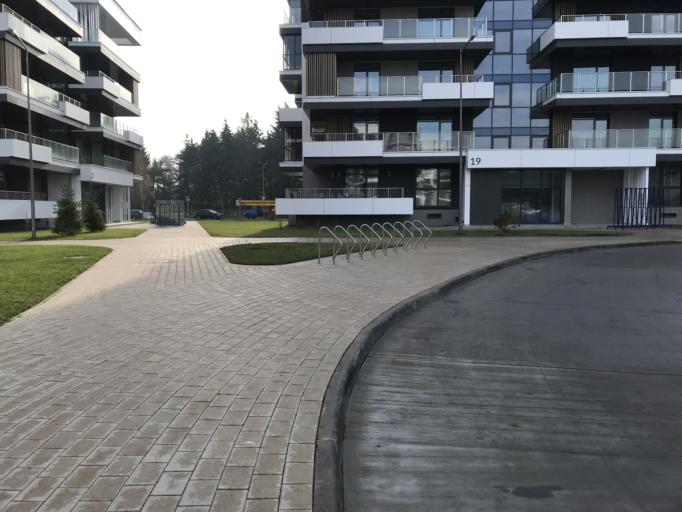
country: BY
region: Minsk
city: Khatsyezhyna
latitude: 53.9464
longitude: 27.3316
